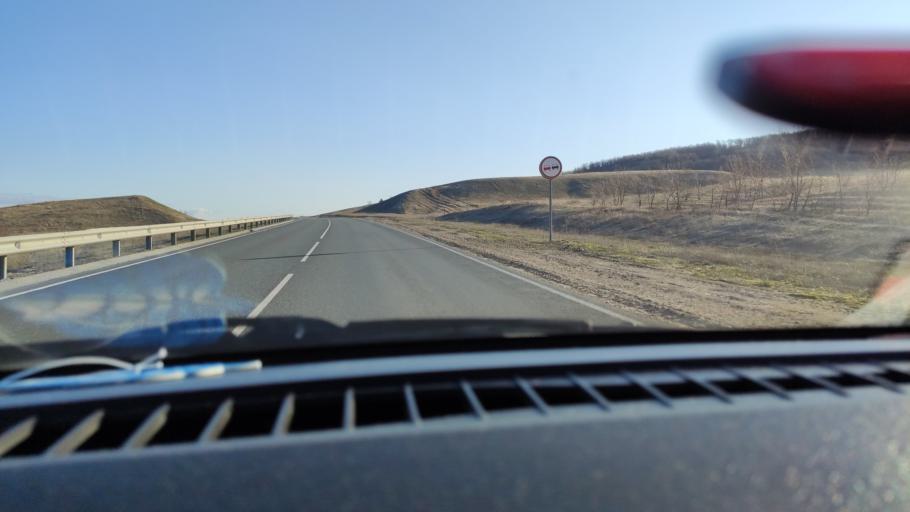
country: RU
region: Saratov
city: Alekseyevka
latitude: 52.3392
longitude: 47.9335
